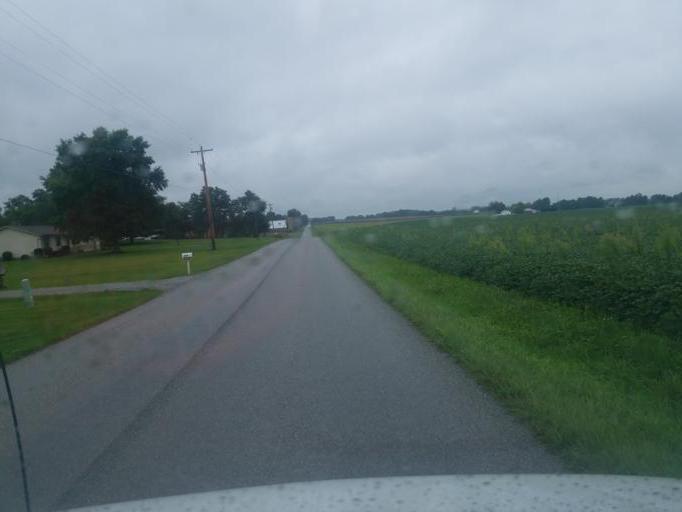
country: US
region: Ohio
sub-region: Medina County
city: Westfield Center
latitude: 40.9741
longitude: -81.9487
